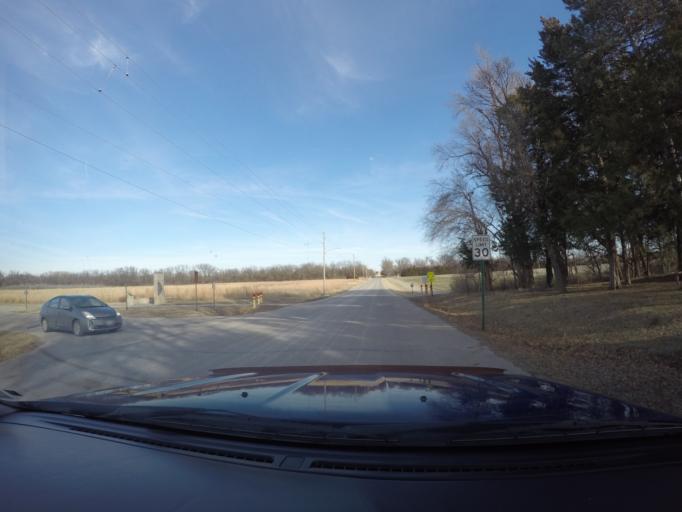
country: US
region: Kansas
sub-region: Harvey County
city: North Newton
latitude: 38.0718
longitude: -97.3395
